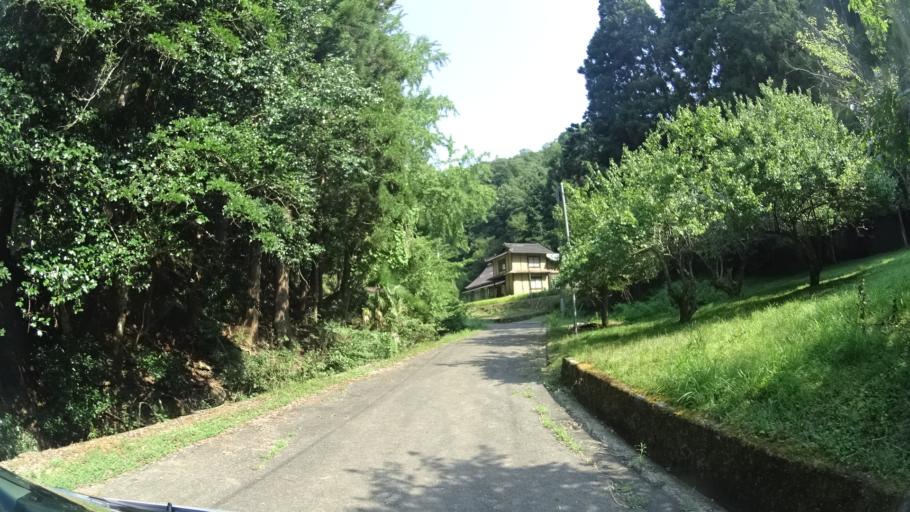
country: JP
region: Kyoto
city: Ayabe
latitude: 35.4009
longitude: 135.2444
